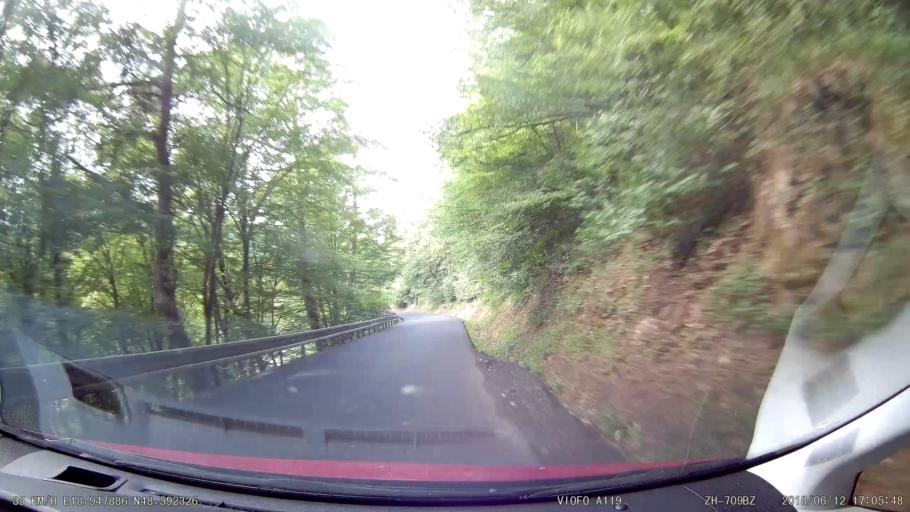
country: SK
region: Banskobystricky
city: Ziar nad Hronom
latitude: 48.5925
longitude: 18.9478
